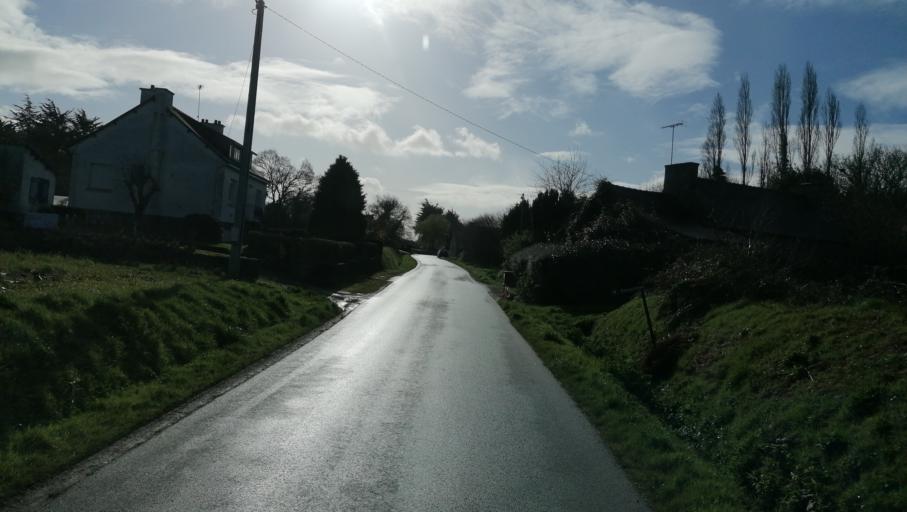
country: FR
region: Brittany
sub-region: Departement des Cotes-d'Armor
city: Plouha
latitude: 48.6510
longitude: -2.9079
